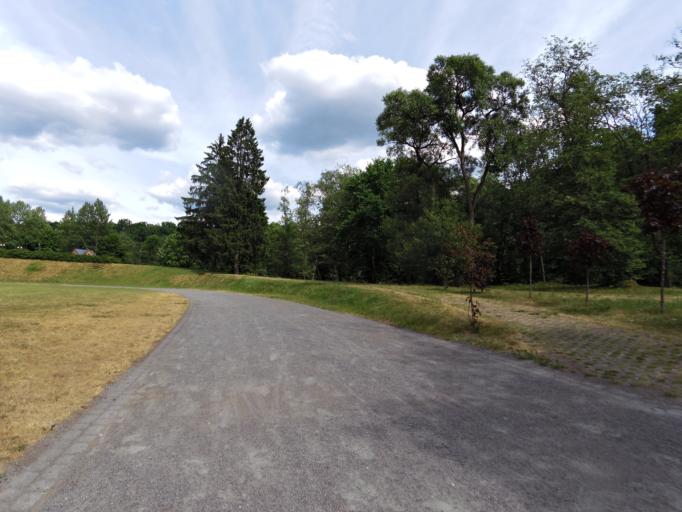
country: LT
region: Vilnius County
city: Rasos
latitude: 54.6827
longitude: 25.3564
